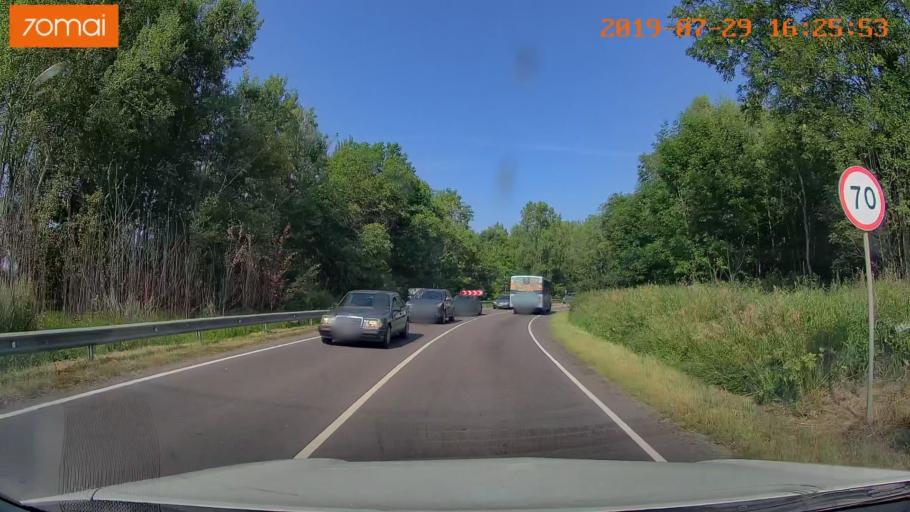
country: RU
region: Kaliningrad
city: Primorsk
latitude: 54.7261
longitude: 19.9703
